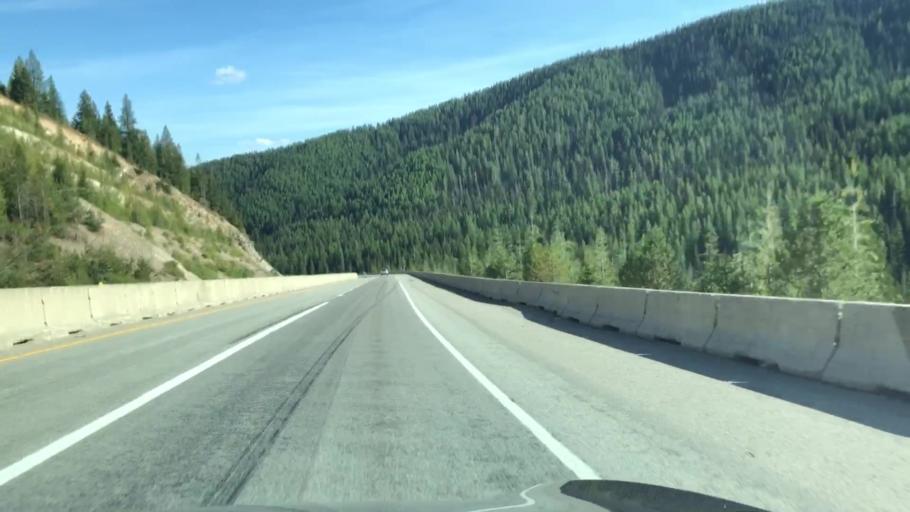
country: US
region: Idaho
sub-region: Shoshone County
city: Wallace
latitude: 47.4396
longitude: -115.6843
